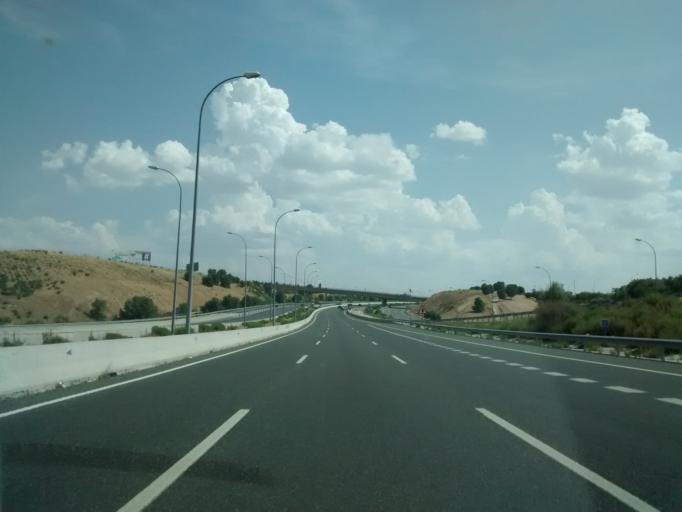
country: ES
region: Madrid
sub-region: Provincia de Madrid
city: Hortaleza
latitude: 40.4937
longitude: -3.6459
